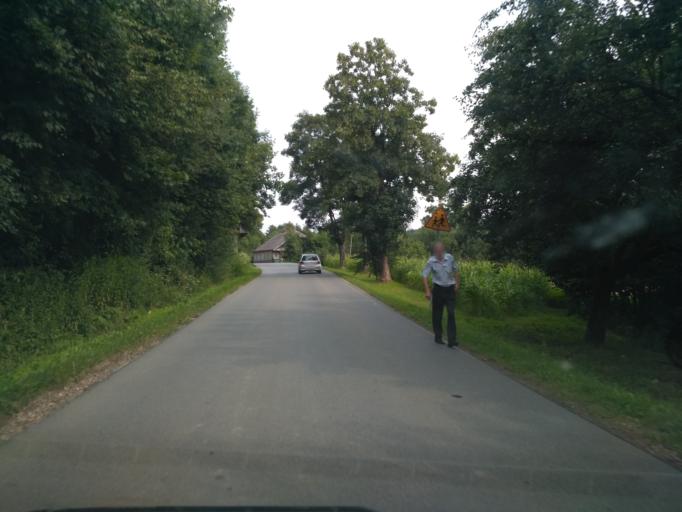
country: PL
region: Subcarpathian Voivodeship
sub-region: Powiat strzyzowski
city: Konieczkowa
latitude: 49.8378
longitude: 21.9539
